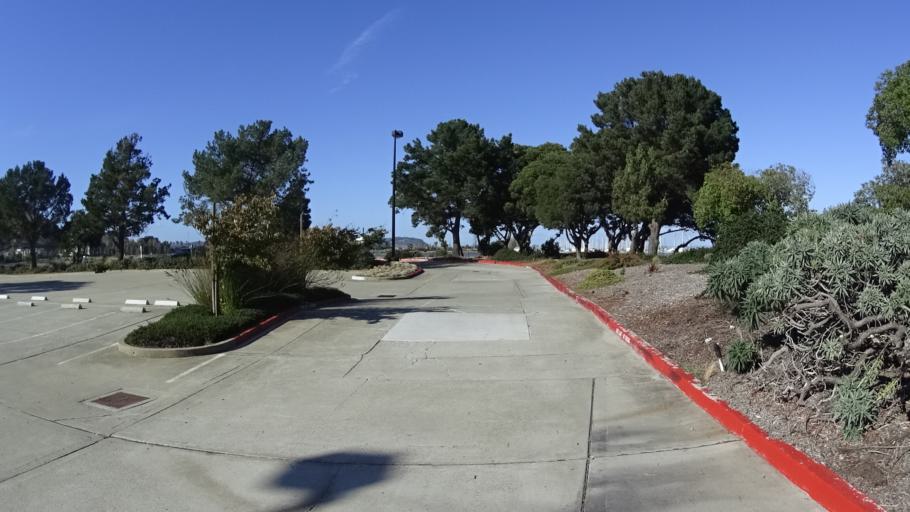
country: US
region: California
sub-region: San Mateo County
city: Brisbane
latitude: 37.6675
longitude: -122.3813
